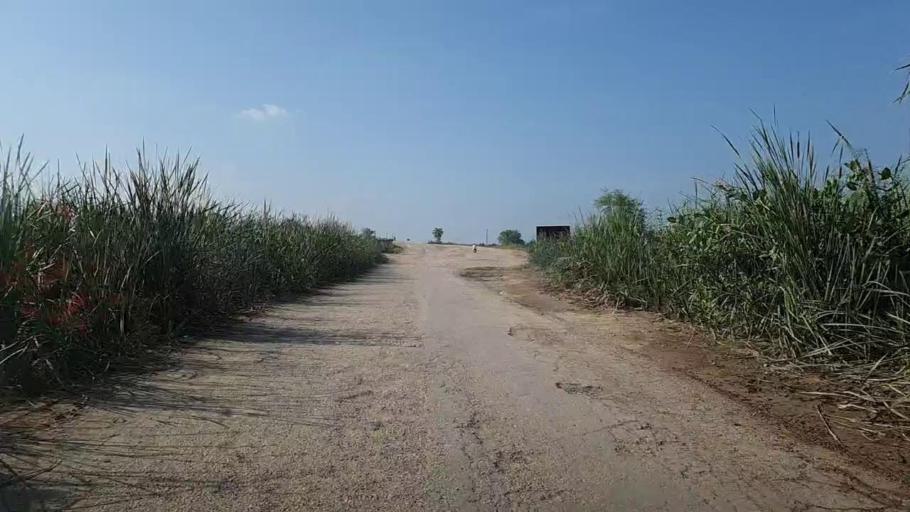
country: PK
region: Sindh
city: Kandiaro
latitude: 27.0704
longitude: 68.3141
